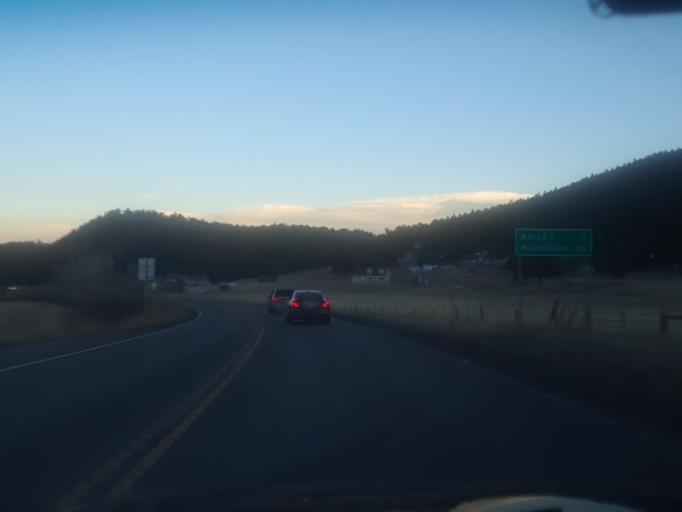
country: US
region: Colorado
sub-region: Jefferson County
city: Evergreen
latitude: 39.4201
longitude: -105.5518
